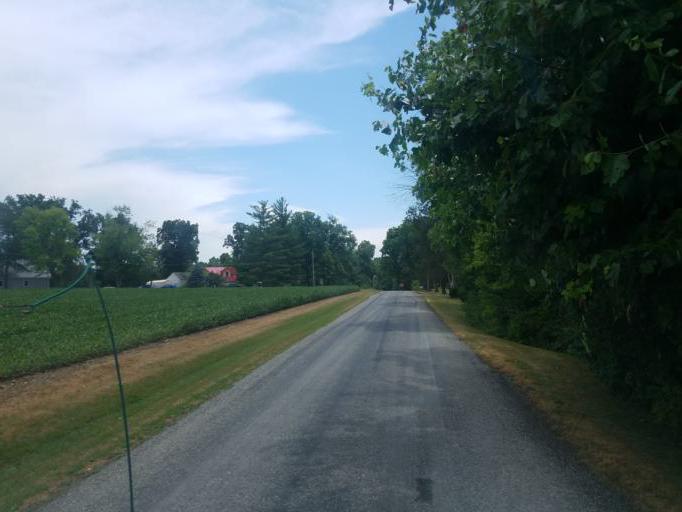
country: US
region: Ohio
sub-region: Paulding County
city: Antwerp
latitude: 41.2019
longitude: -84.7275
